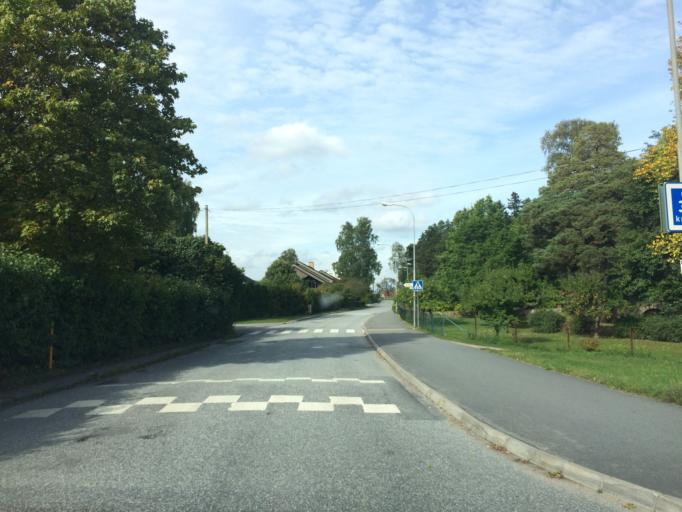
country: SE
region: Stockholm
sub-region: Sollentuna Kommun
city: Sollentuna
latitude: 59.4370
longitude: 17.9483
